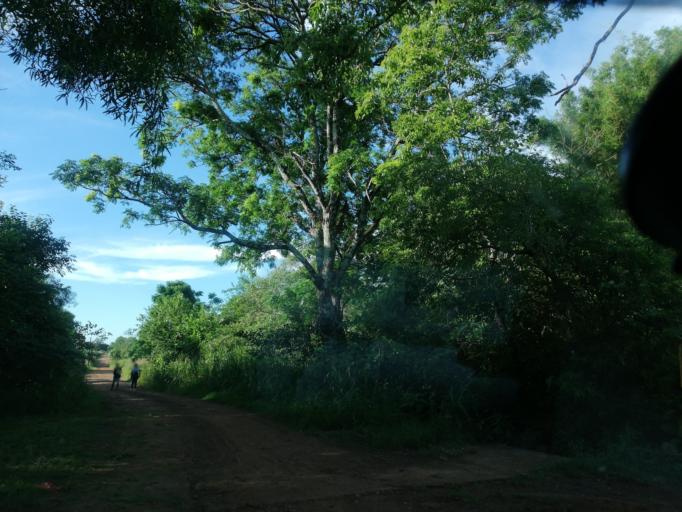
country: AR
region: Misiones
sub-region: Departamento de Capital
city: Posadas
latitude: -27.4032
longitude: -55.9588
